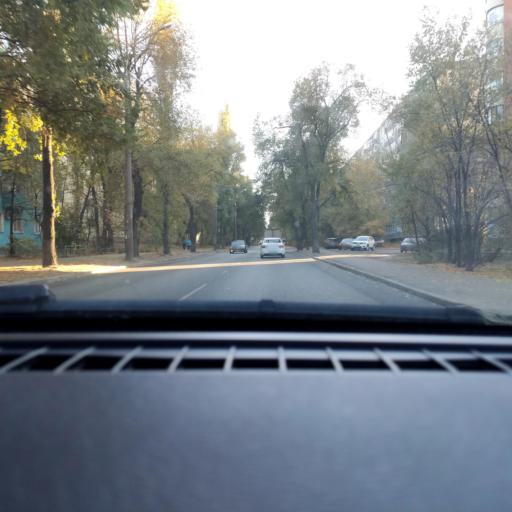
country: RU
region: Voronezj
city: Voronezh
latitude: 51.6942
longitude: 39.2632
